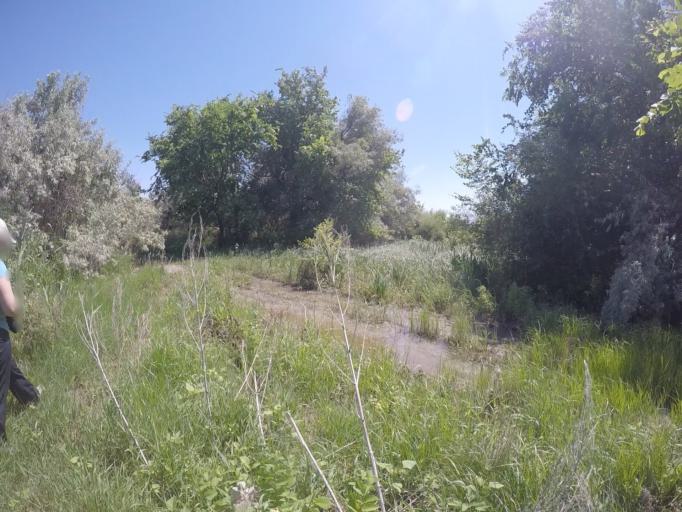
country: RU
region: Saratov
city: Krasnoarmeysk
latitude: 51.1526
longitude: 45.9039
